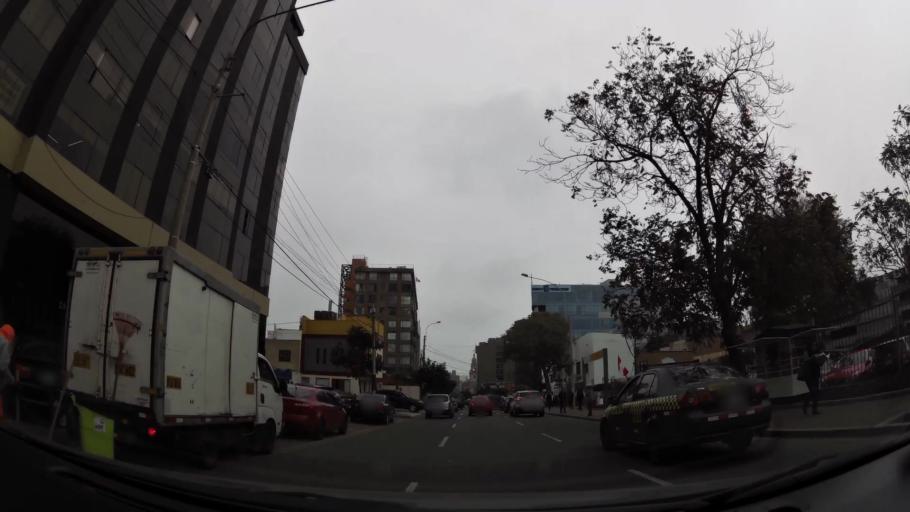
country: PE
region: Lima
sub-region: Lima
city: San Isidro
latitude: -12.0933
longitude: -77.0346
